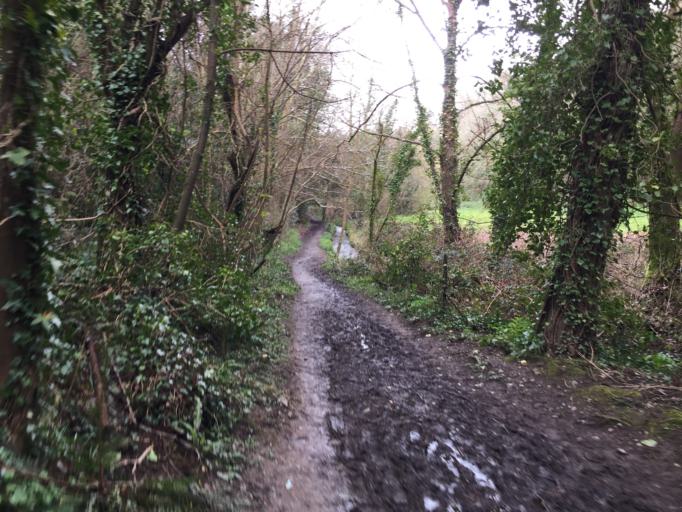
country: JE
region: St Helier
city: Saint Helier
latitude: 49.2119
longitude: -2.1327
